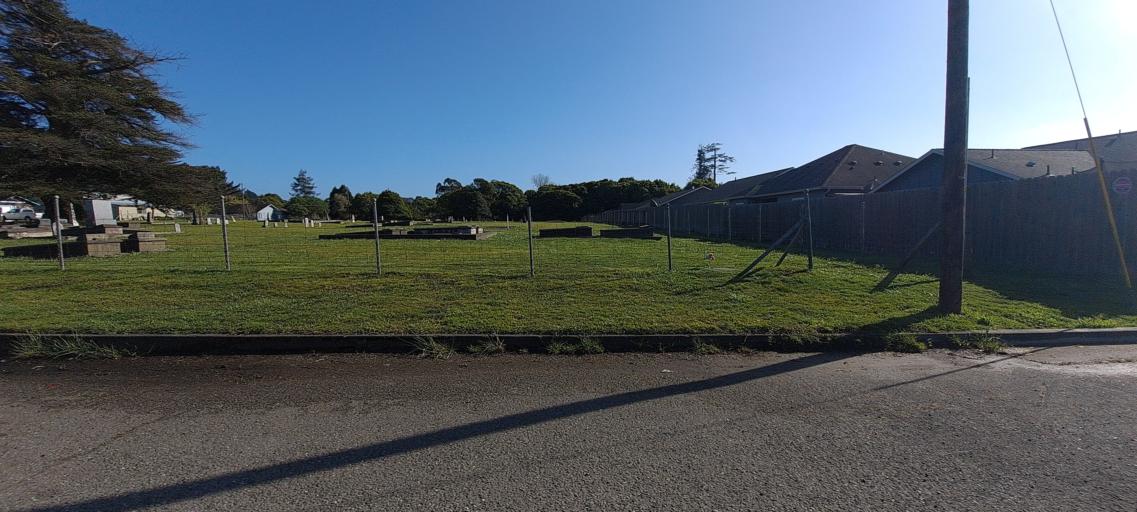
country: US
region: California
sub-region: Humboldt County
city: Fortuna
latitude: 40.5739
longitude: -124.1338
